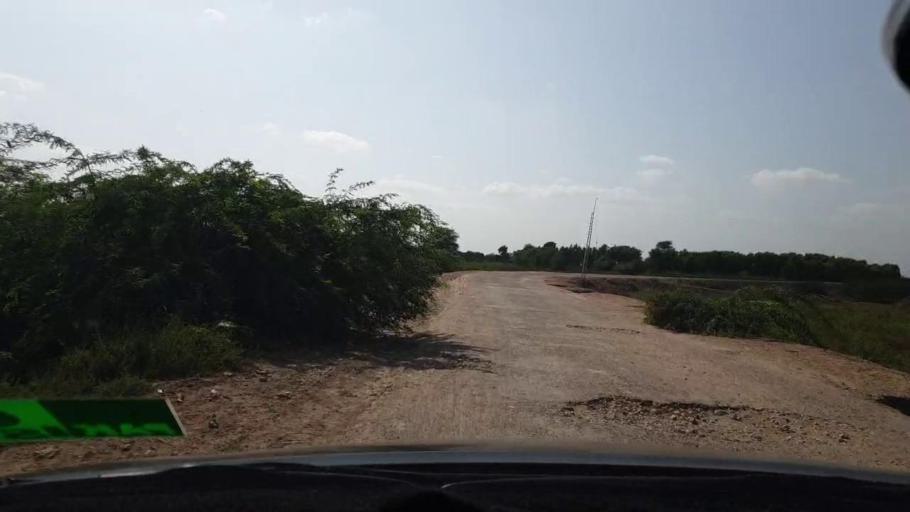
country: PK
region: Sindh
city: Tando Bago
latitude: 24.6623
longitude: 69.2035
